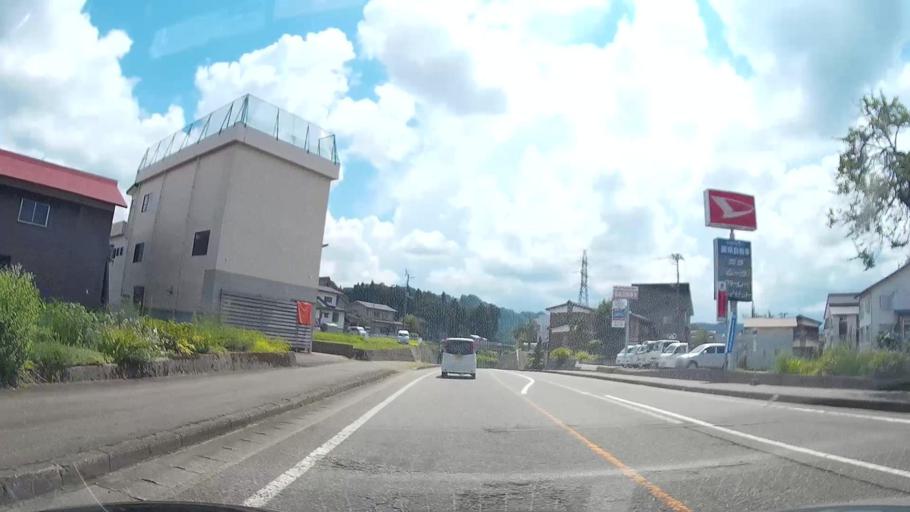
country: JP
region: Niigata
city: Tokamachi
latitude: 37.0193
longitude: 138.6556
